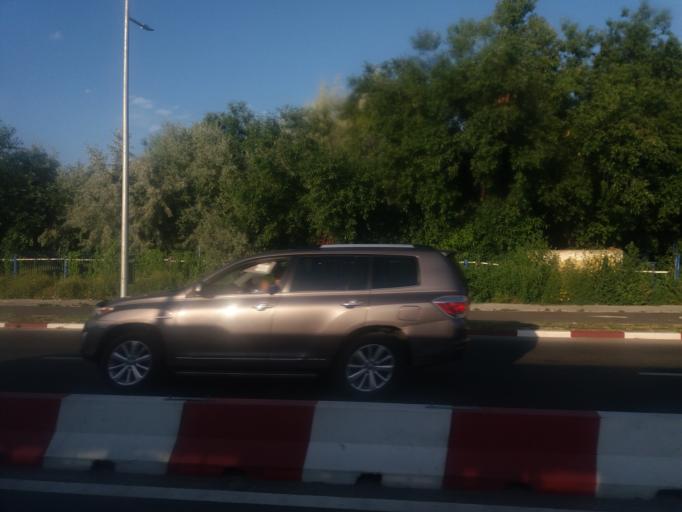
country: RO
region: Constanta
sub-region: Comuna Navodari
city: Navodari
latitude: 44.2755
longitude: 28.6176
